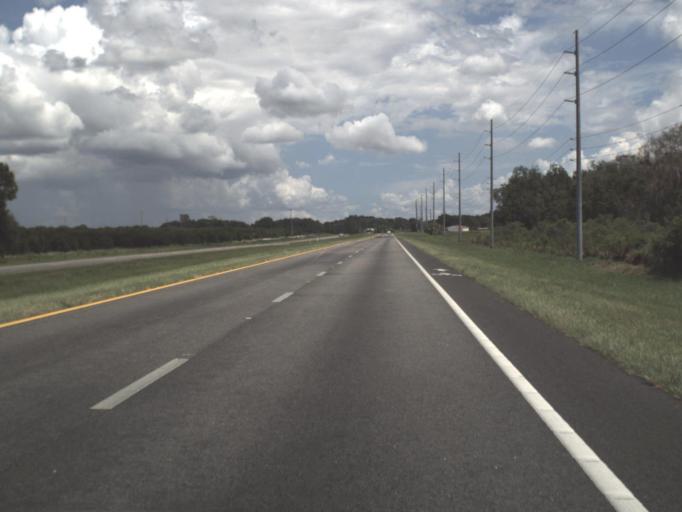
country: US
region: Florida
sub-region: Polk County
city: Lake Wales
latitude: 27.9006
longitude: -81.6386
